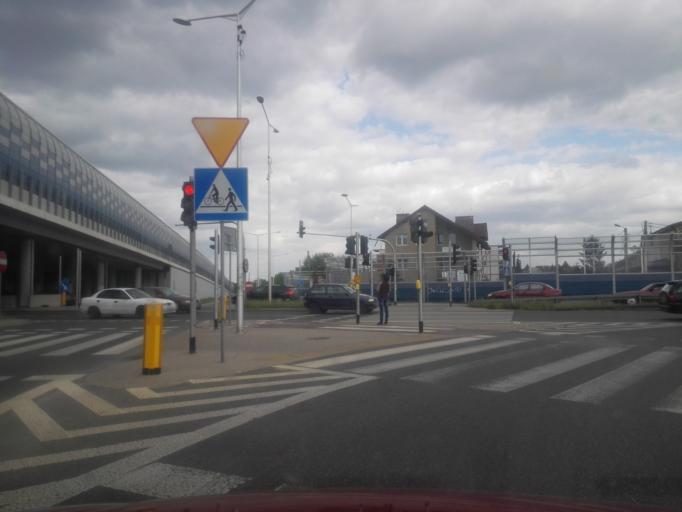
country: PL
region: Masovian Voivodeship
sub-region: Powiat wolominski
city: Marki
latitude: 52.3072
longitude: 21.0915
